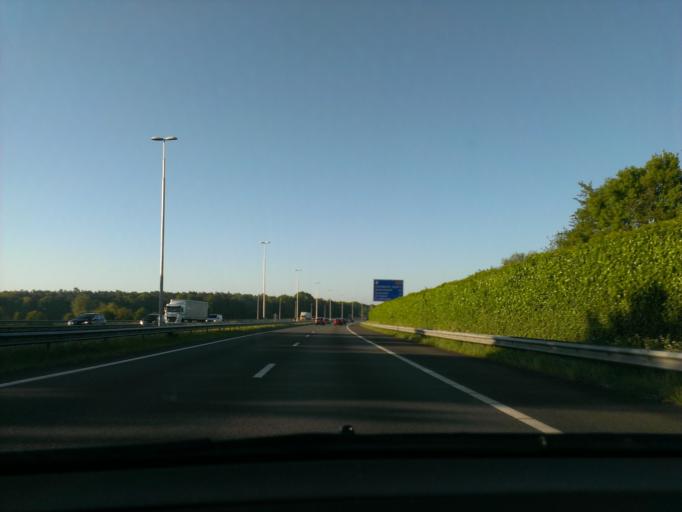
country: NL
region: Gelderland
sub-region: Gemeente Apeldoorn
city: Apeldoorn
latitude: 52.2180
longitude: 6.0221
